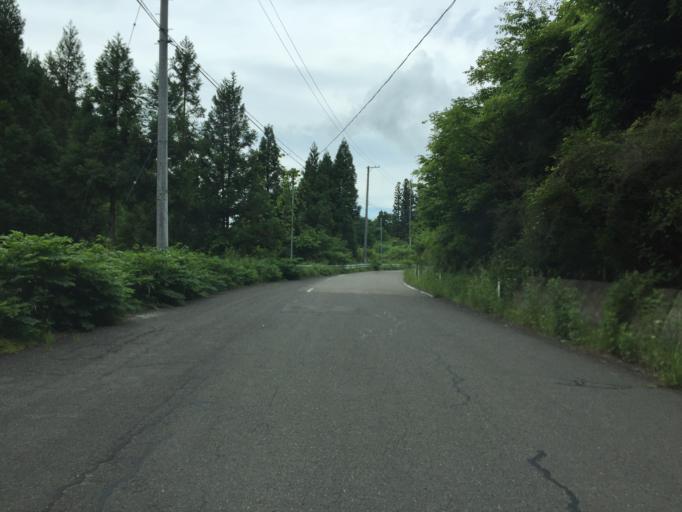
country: JP
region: Fukushima
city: Funehikimachi-funehiki
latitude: 37.4261
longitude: 140.7363
